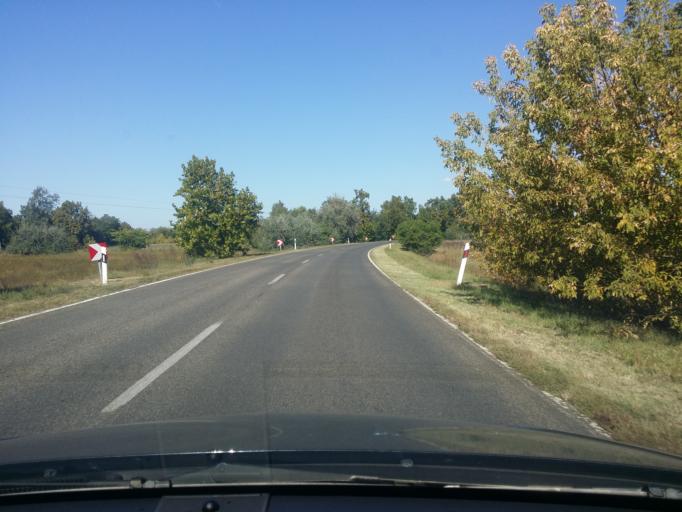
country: HU
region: Csongrad
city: Kistelek
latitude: 46.4893
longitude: 19.9628
